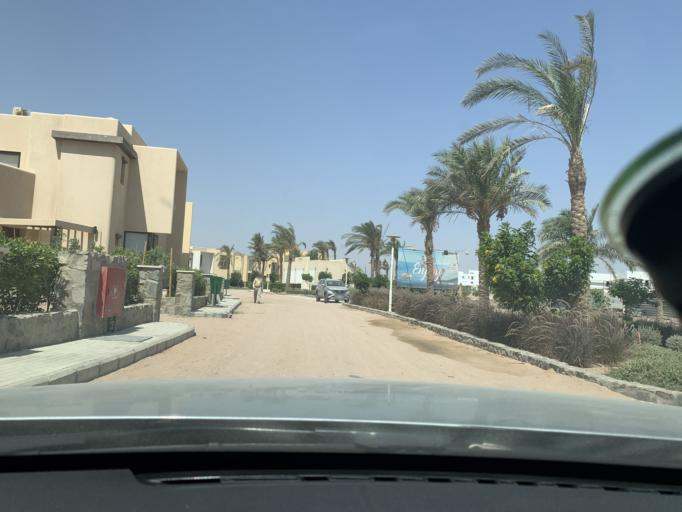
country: EG
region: Red Sea
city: El Gouna
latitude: 27.4037
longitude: 33.6633
